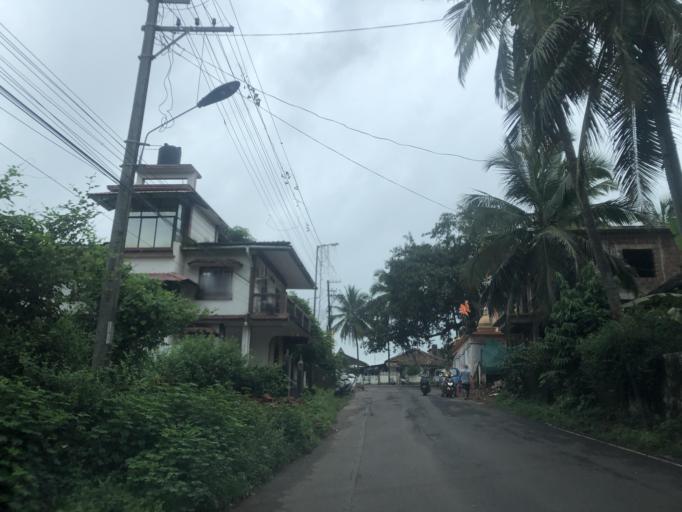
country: IN
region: Goa
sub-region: North Goa
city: Serula
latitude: 15.5476
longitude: 73.8257
